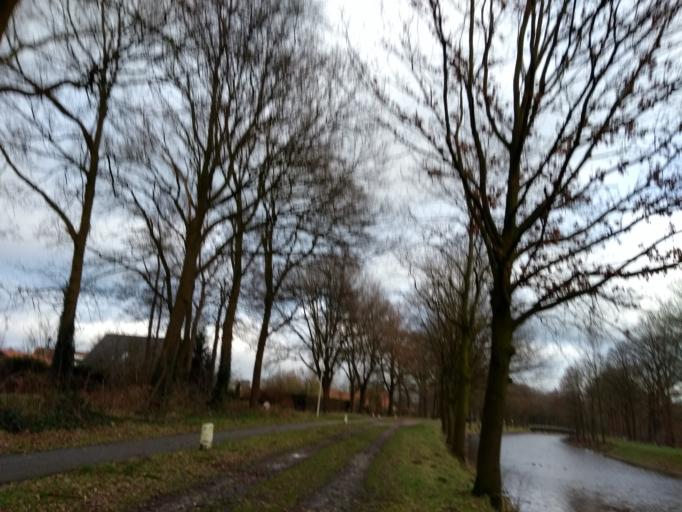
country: NL
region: Overijssel
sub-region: Gemeente Almelo
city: Almelo
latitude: 52.3691
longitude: 6.7010
